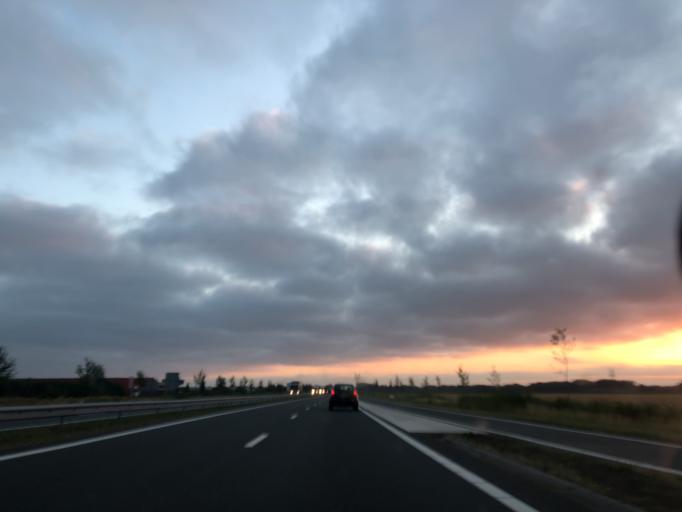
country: NL
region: Groningen
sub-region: Gemeente Veendam
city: Veendam
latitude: 53.0785
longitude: 6.8829
